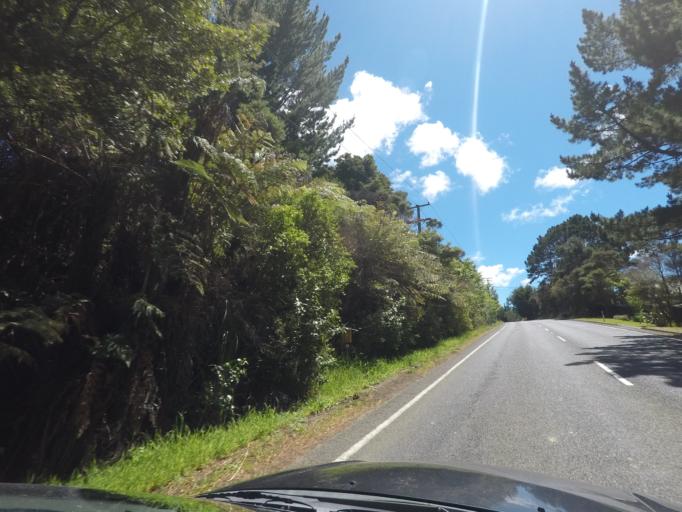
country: NZ
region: Auckland
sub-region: Auckland
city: Rothesay Bay
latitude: -36.7407
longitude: 174.6749
